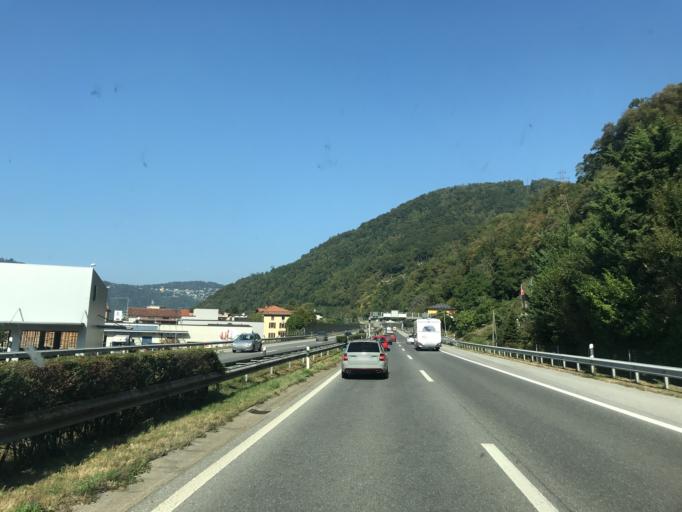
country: CH
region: Ticino
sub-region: Lugano District
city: Melano
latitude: 45.9316
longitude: 8.9764
